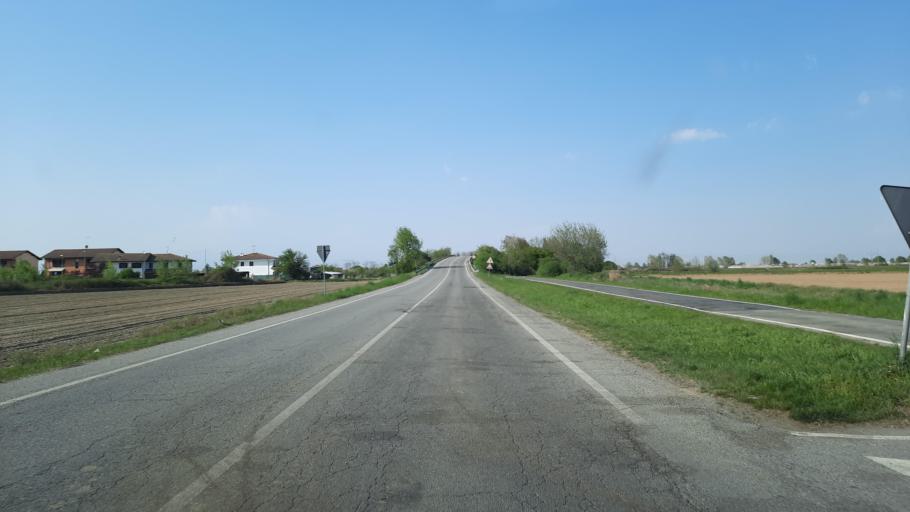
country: IT
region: Piedmont
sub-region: Provincia di Vercelli
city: Crescentino
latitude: 45.1911
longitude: 8.1151
